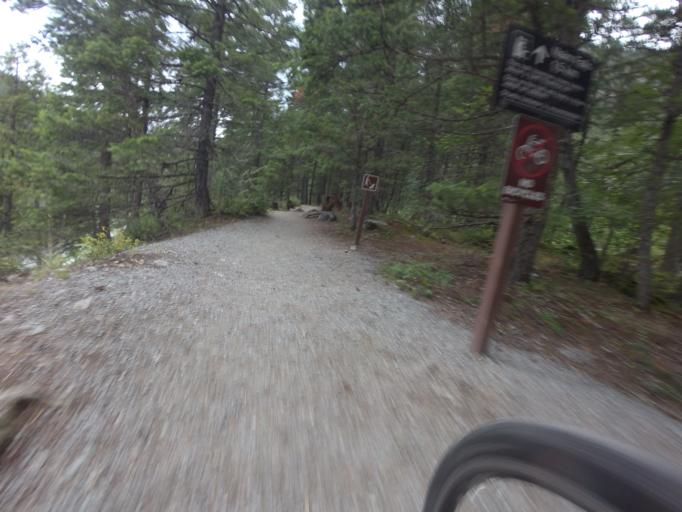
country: CA
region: British Columbia
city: Pemberton
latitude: 50.2964
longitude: -122.8213
